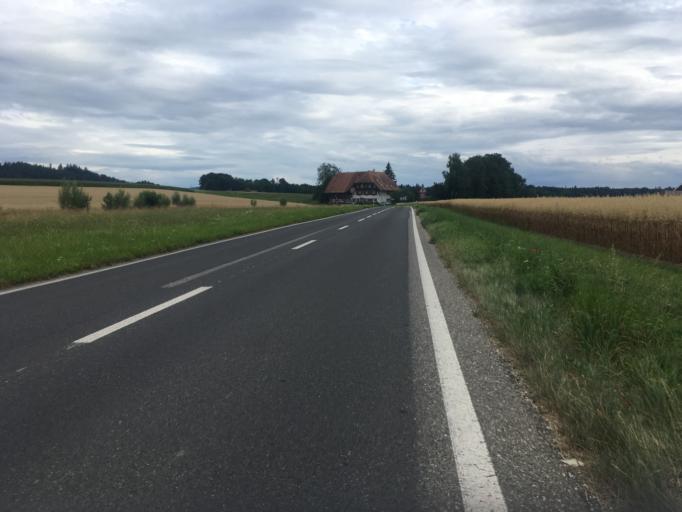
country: CH
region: Bern
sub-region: Seeland District
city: Erlach
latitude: 47.0351
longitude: 7.0942
